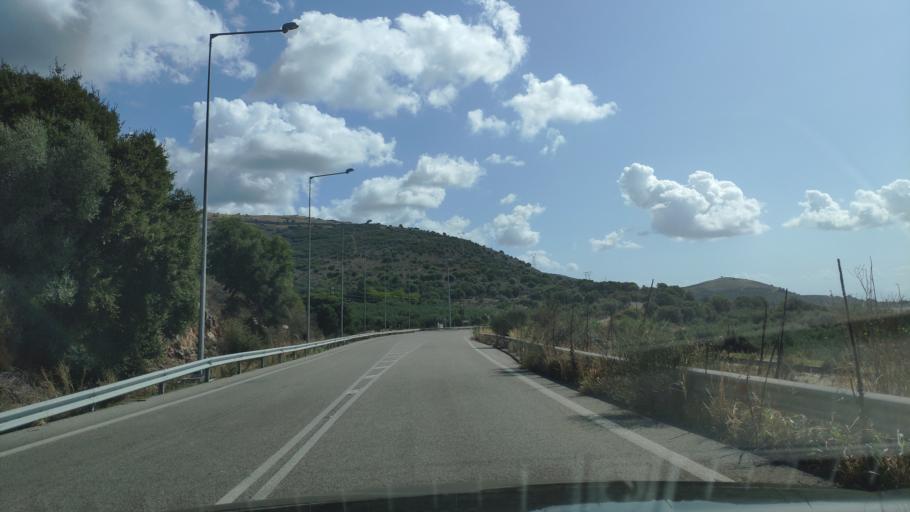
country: GR
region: West Greece
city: Aitoliko
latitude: 38.4132
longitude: 21.3933
